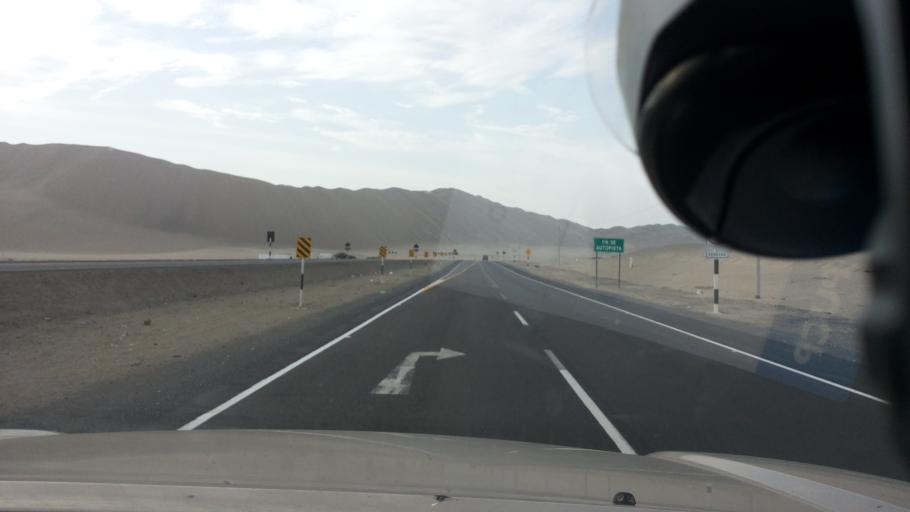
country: PE
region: Ancash
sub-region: Provincia de Casma
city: Casma
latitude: -9.5227
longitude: -78.2847
